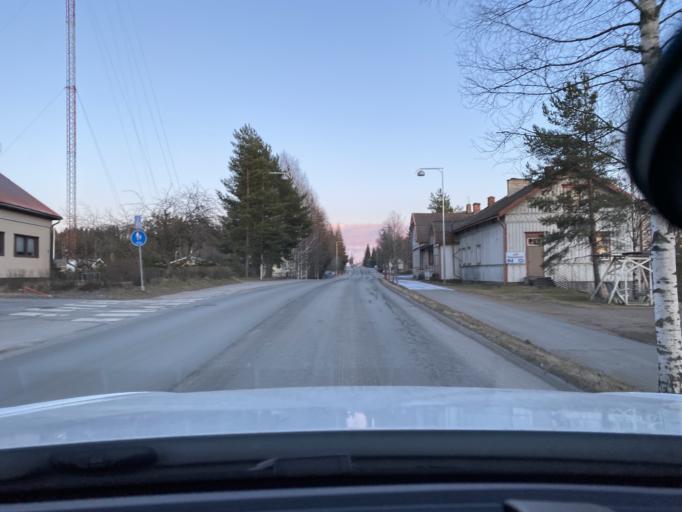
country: FI
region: Pirkanmaa
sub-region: Lounais-Pirkanmaa
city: Punkalaidun
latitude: 61.1160
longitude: 23.0907
